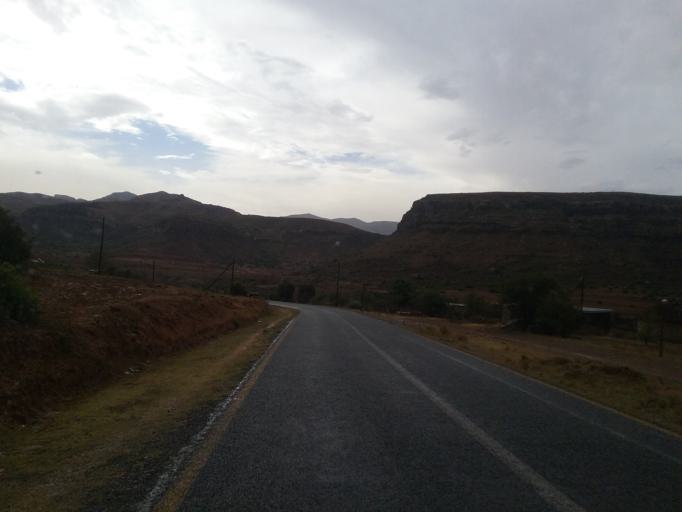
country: LS
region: Quthing
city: Quthing
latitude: -30.3385
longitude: 27.7386
